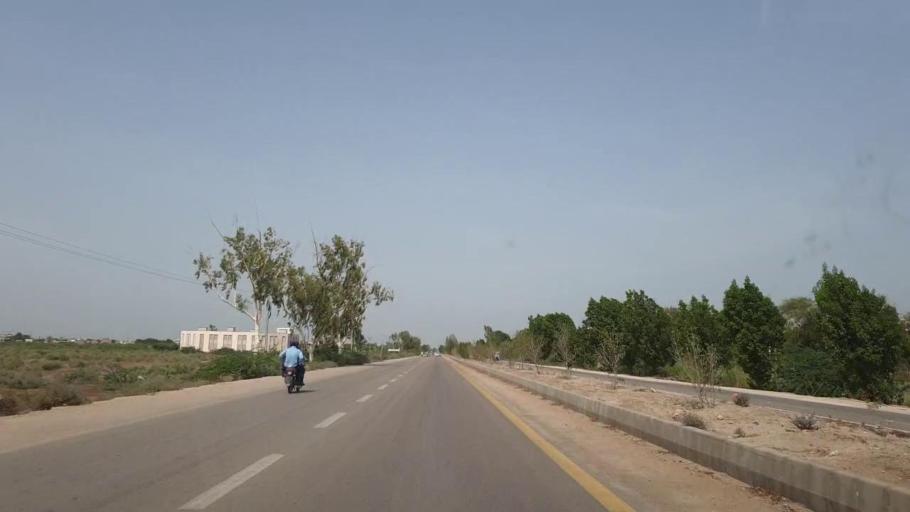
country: PK
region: Sindh
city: Nawabshah
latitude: 26.2316
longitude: 68.3745
